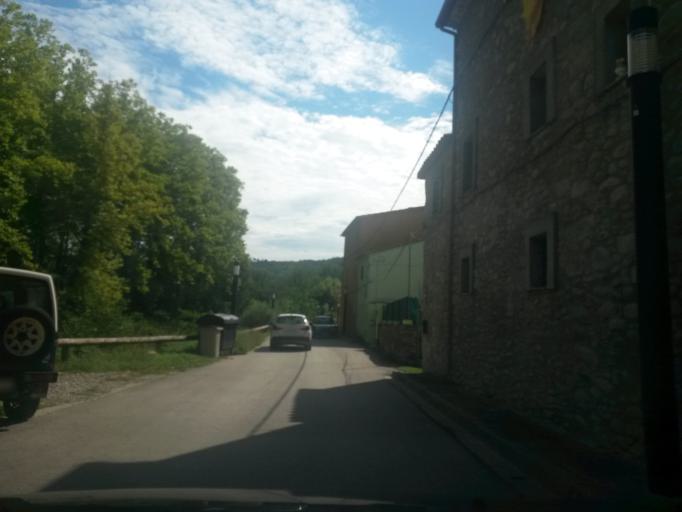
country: ES
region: Catalonia
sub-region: Provincia de Girona
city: la Cellera de Ter
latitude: 41.9864
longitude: 2.6156
